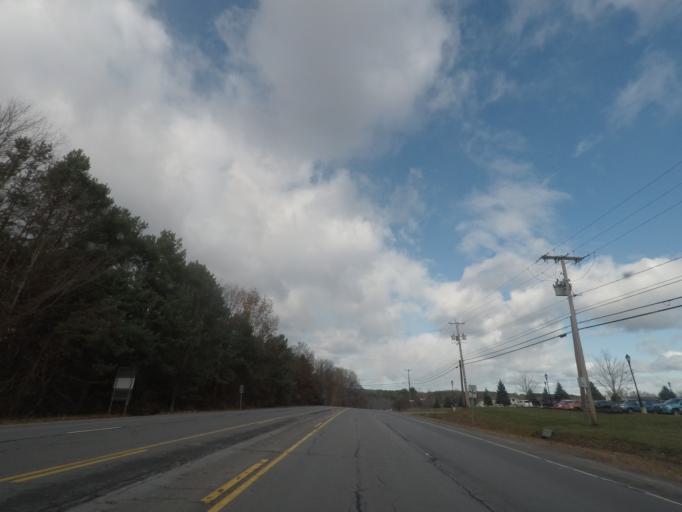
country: US
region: New York
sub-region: Saratoga County
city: Ballston Spa
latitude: 42.9951
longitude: -73.7909
